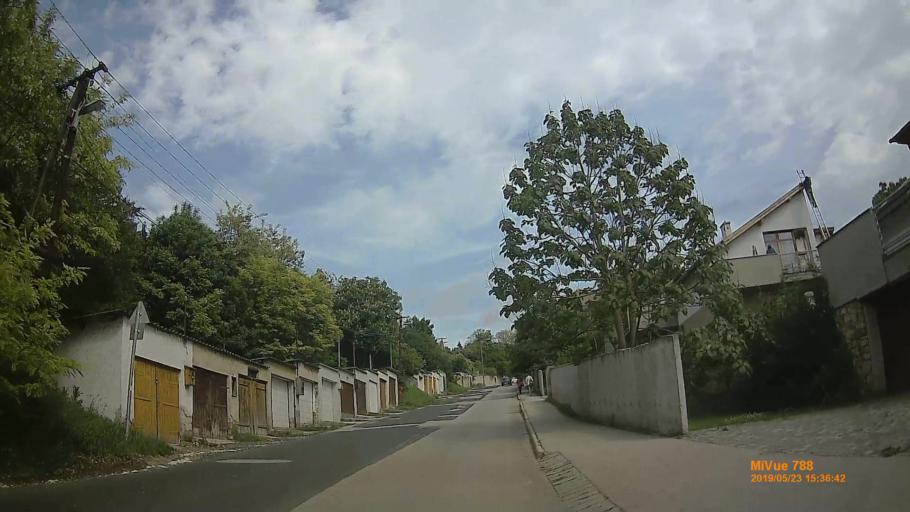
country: HU
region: Veszprem
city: Veszprem
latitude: 47.0983
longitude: 17.9099
